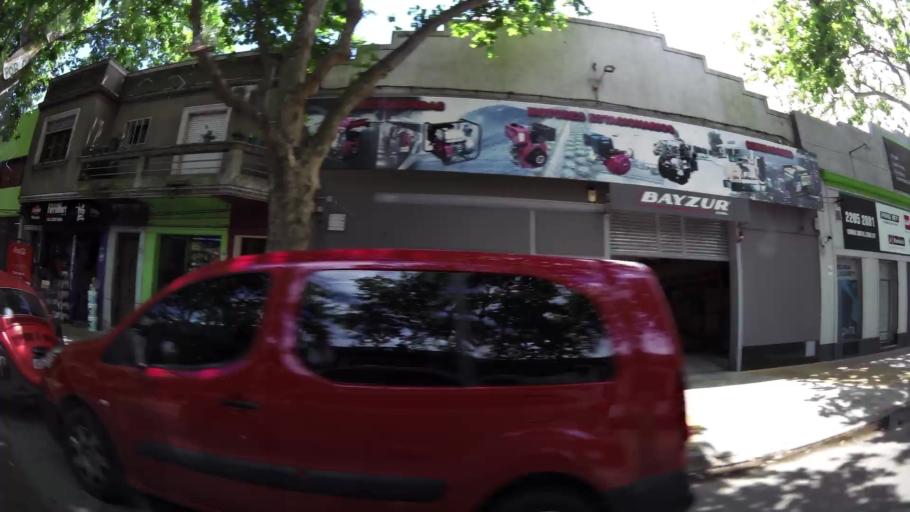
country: UY
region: Montevideo
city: Montevideo
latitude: -34.8744
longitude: -56.1844
